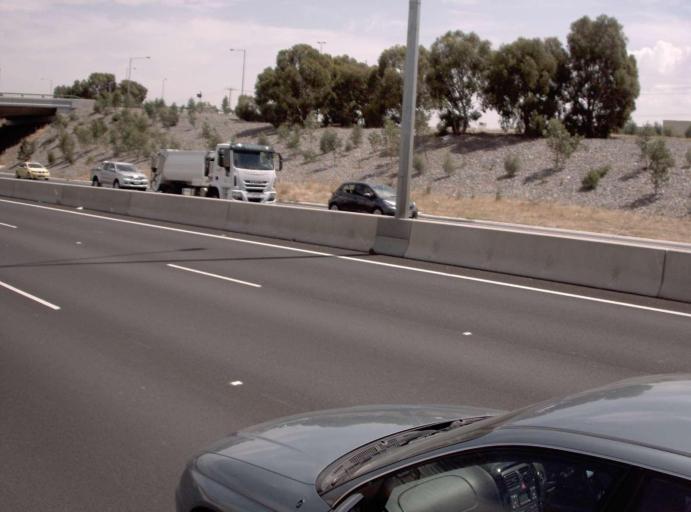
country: AU
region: Victoria
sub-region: Moonee Valley
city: Airport West
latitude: -37.7151
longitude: 144.8766
